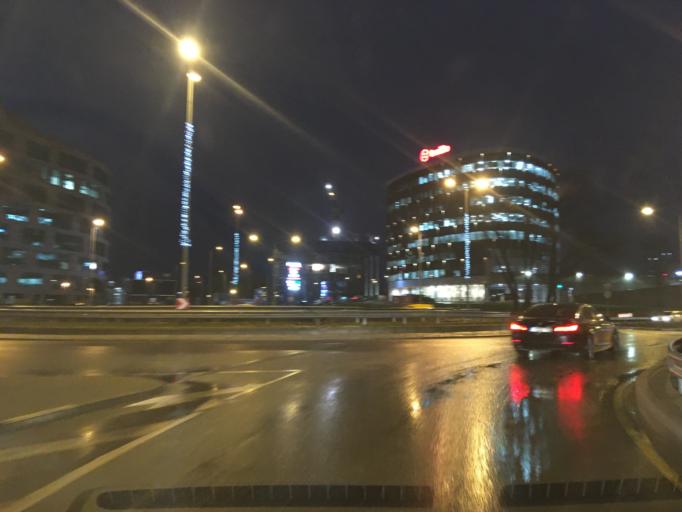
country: EE
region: Harju
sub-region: Tallinna linn
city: Tallinn
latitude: 59.4191
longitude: 24.7515
